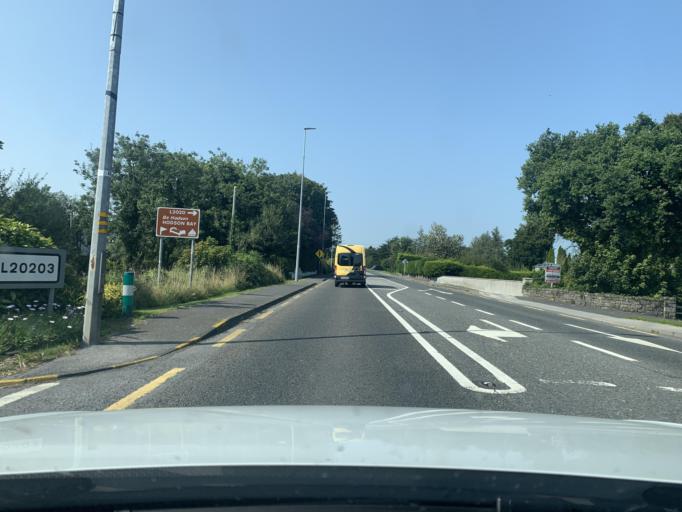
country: IE
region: Leinster
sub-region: An Iarmhi
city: Athlone
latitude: 53.4559
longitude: -7.9955
